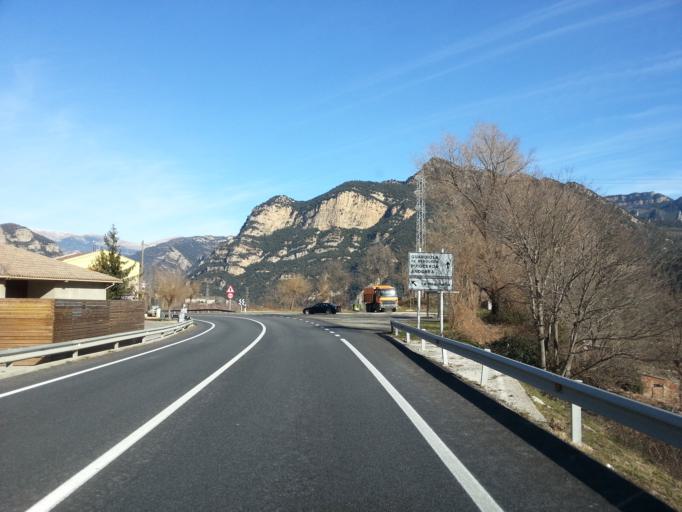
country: ES
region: Catalonia
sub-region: Provincia de Barcelona
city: Vallcebre
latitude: 42.1631
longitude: 1.8560
